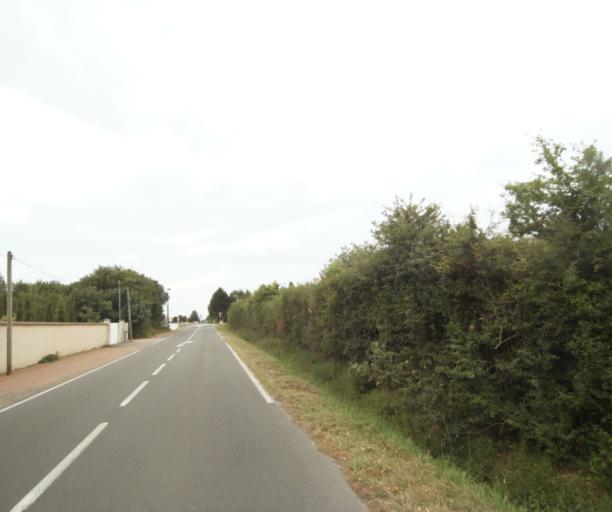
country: FR
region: Pays de la Loire
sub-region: Departement de la Vendee
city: Chateau-d'Olonne
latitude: 46.4784
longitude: -1.7183
